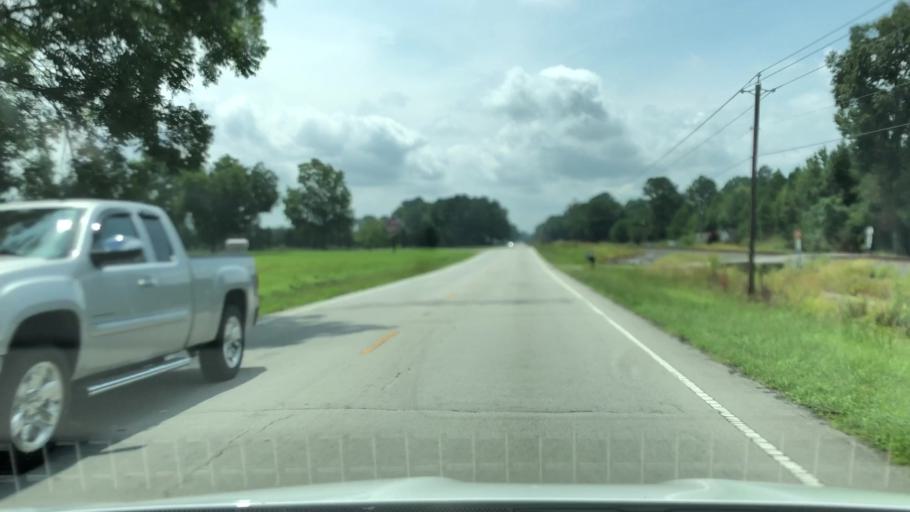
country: US
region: North Carolina
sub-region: Craven County
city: Vanceboro
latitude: 35.3441
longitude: -77.1510
